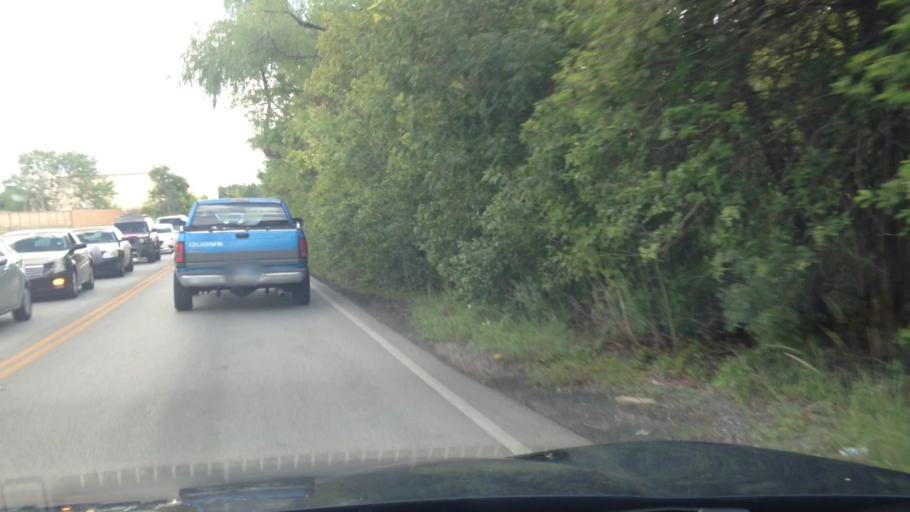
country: US
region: Texas
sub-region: Bexar County
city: Windcrest
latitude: 29.5757
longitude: -98.3996
